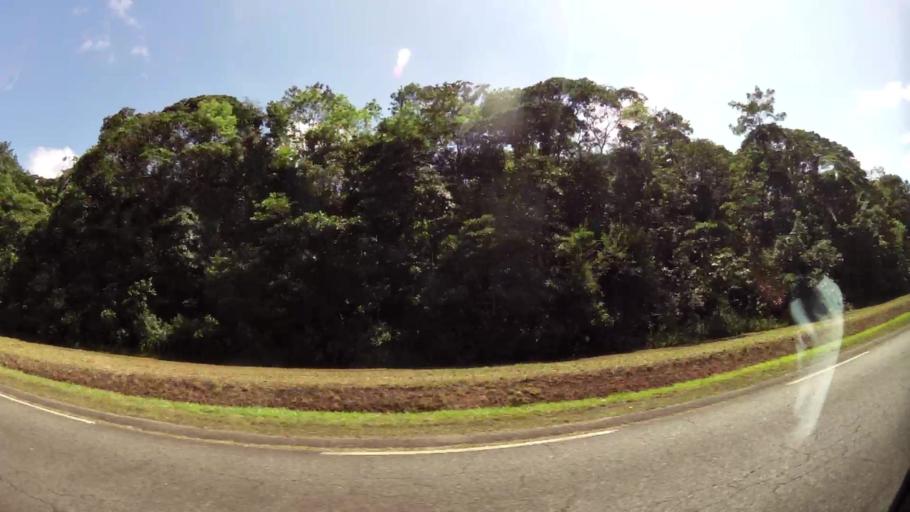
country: GF
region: Guyane
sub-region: Guyane
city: Matoury
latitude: 4.8361
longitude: -52.3342
